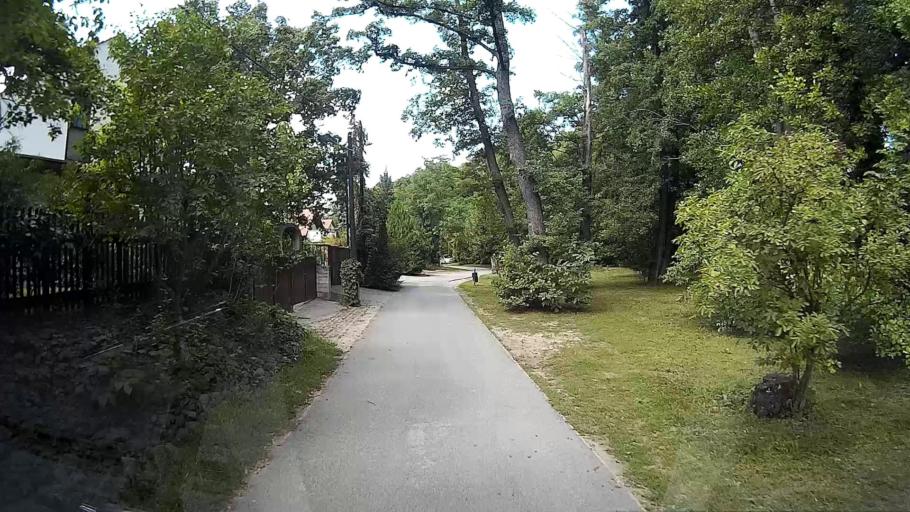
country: HU
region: Pest
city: Szentendre
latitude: 47.6707
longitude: 19.0650
